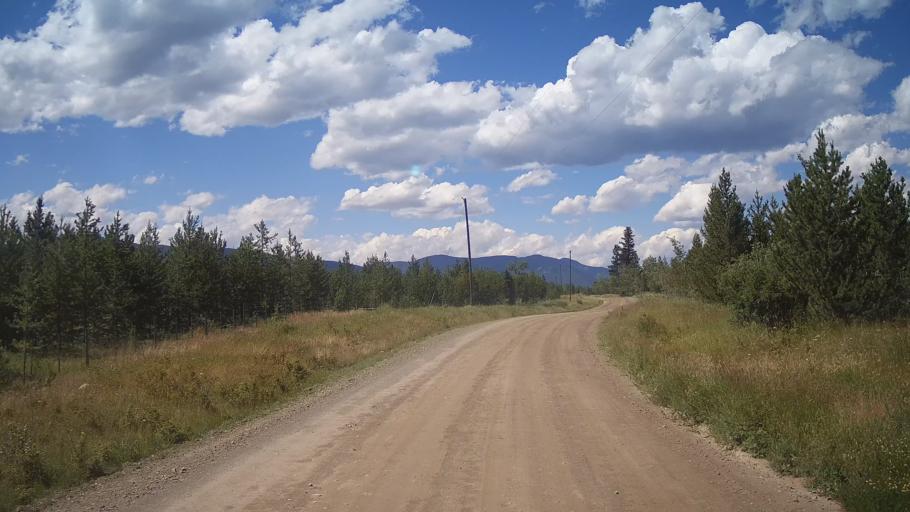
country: CA
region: British Columbia
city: Cache Creek
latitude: 51.2699
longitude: -121.7202
